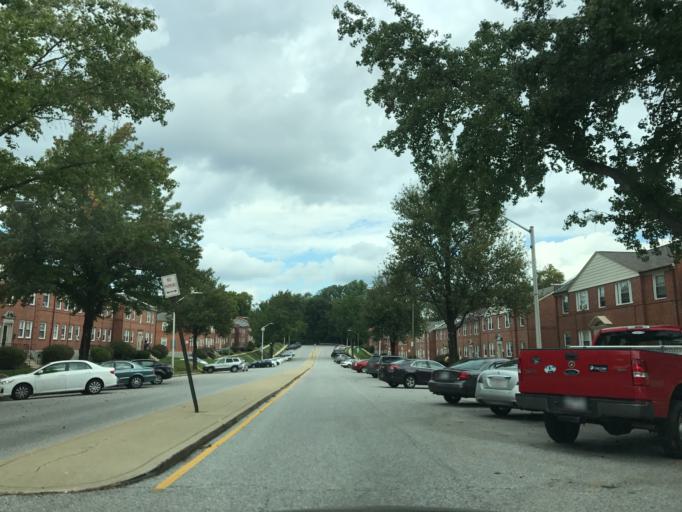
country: US
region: Maryland
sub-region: Baltimore County
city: Lochearn
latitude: 39.3289
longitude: -76.6655
